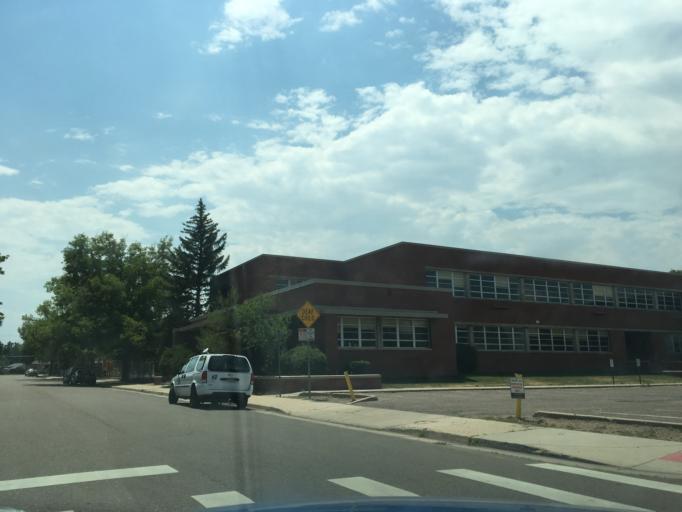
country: US
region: Colorado
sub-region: Arapahoe County
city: Sheridan
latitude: 39.6841
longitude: -105.0282
